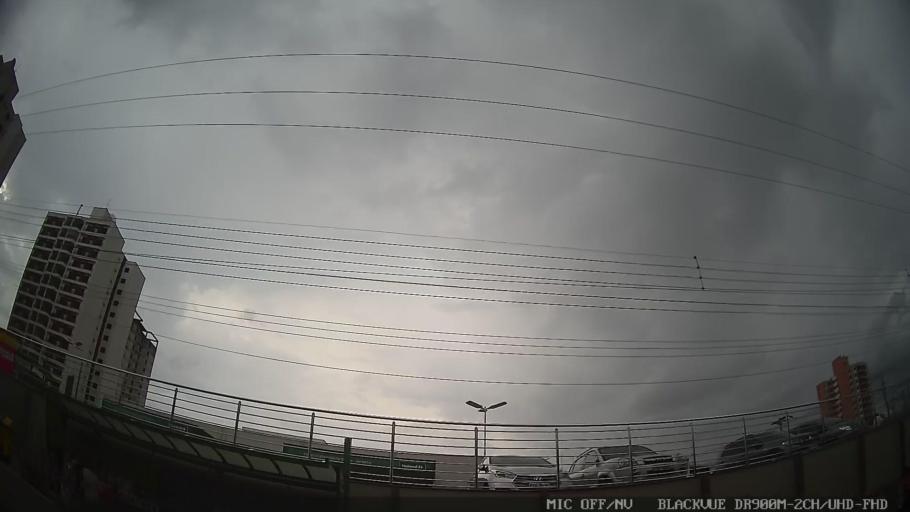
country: BR
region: Sao Paulo
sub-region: Amparo
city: Amparo
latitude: -22.7075
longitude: -46.7732
